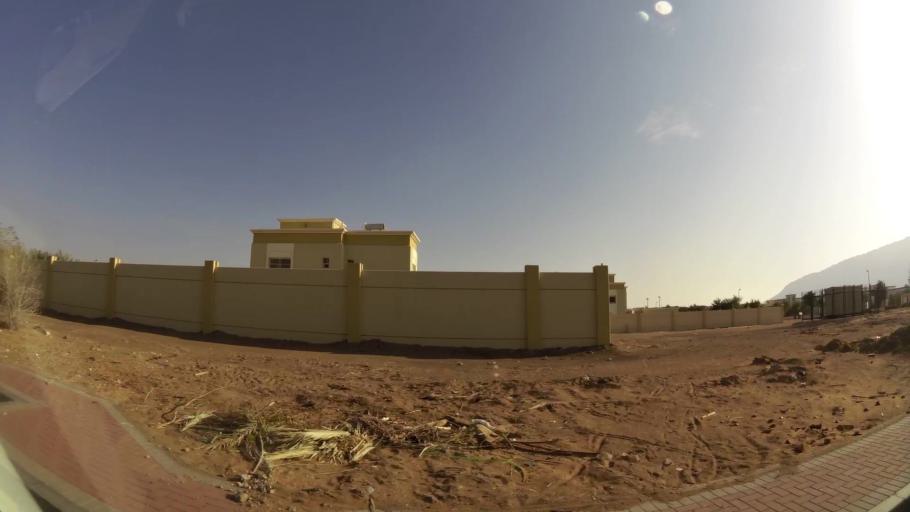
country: AE
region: Abu Dhabi
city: Al Ain
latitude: 24.0578
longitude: 55.8438
